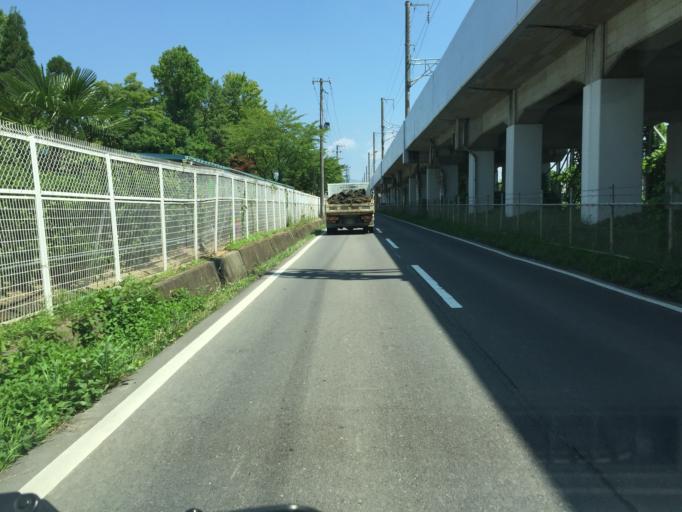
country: JP
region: Fukushima
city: Fukushima-shi
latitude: 37.7296
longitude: 140.4566
